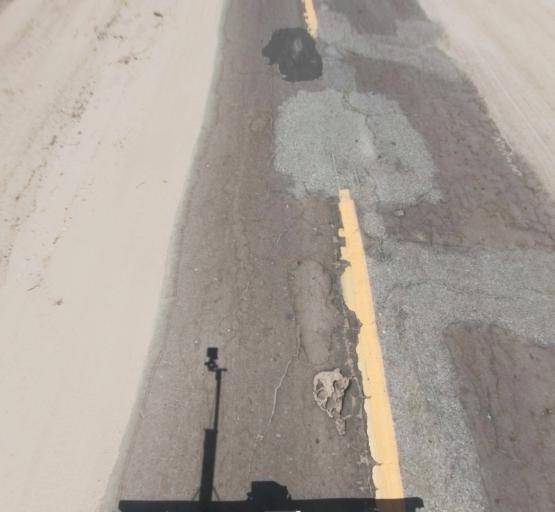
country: US
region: California
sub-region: Fresno County
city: Kerman
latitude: 36.8222
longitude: -120.1465
